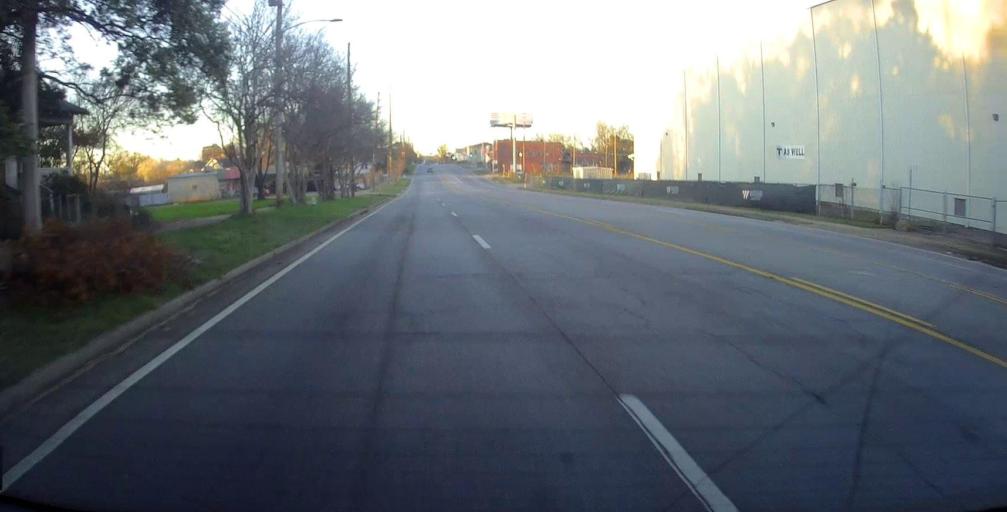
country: US
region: Alabama
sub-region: Russell County
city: Phenix City
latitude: 32.4949
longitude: -84.9902
